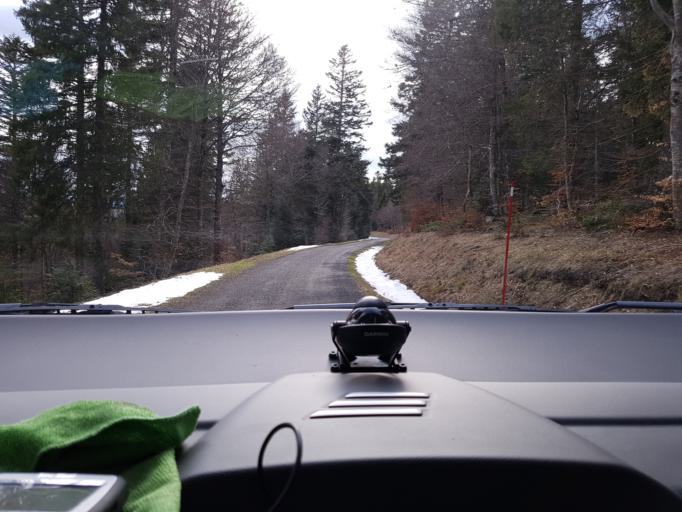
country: FR
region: Midi-Pyrenees
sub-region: Departement de l'Aveyron
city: Laguiole
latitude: 44.6507
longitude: 2.9448
